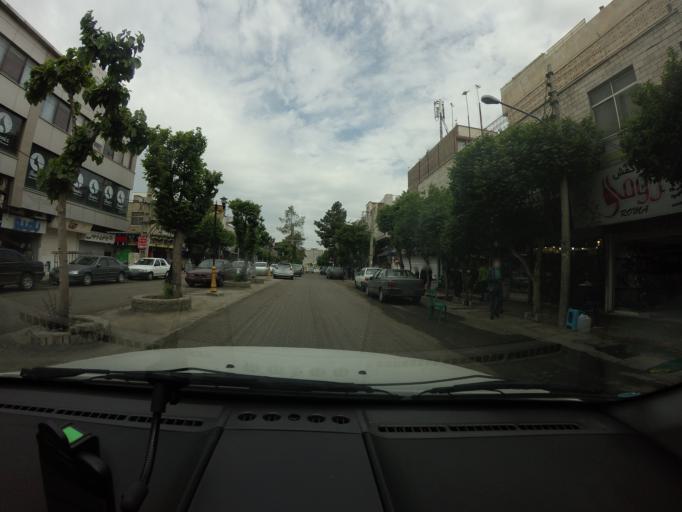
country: IR
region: Tehran
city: Eslamshahr
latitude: 35.5568
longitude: 51.2470
